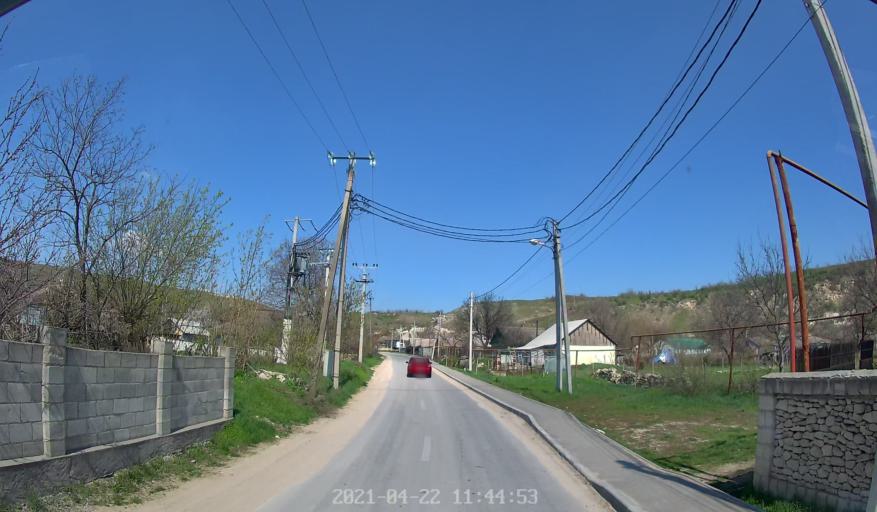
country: MD
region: Chisinau
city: Ciorescu
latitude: 47.1459
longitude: 28.8961
